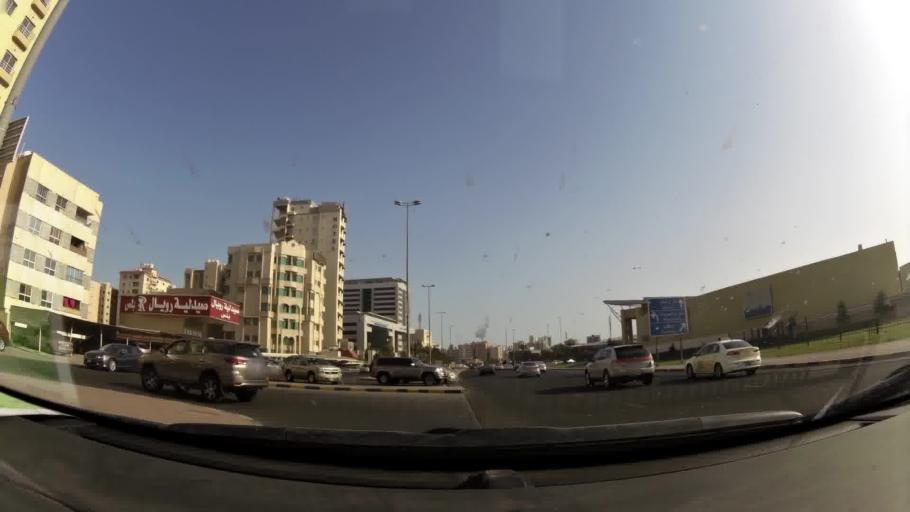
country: KW
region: Muhafazat Hawalli
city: As Salimiyah
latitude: 29.3306
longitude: 48.0771
